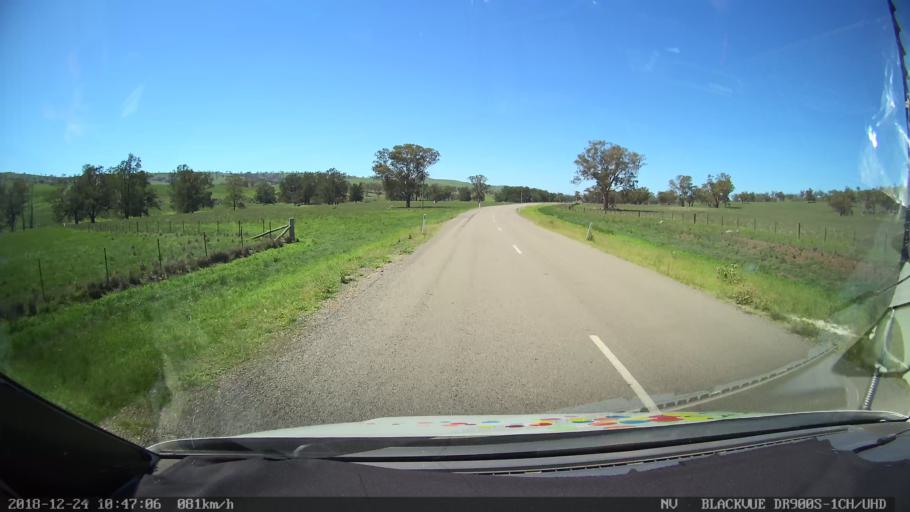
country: AU
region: New South Wales
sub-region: Upper Hunter Shire
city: Merriwa
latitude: -31.9202
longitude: 150.4292
